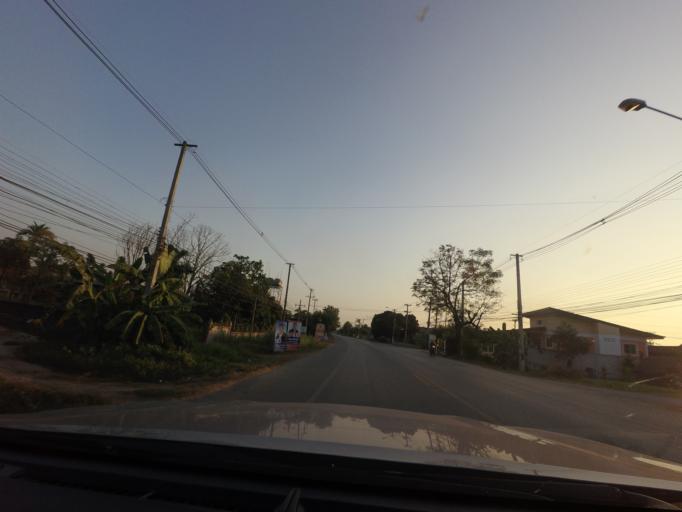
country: TH
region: Sukhothai
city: Si Samrong
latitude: 17.1392
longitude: 99.8499
